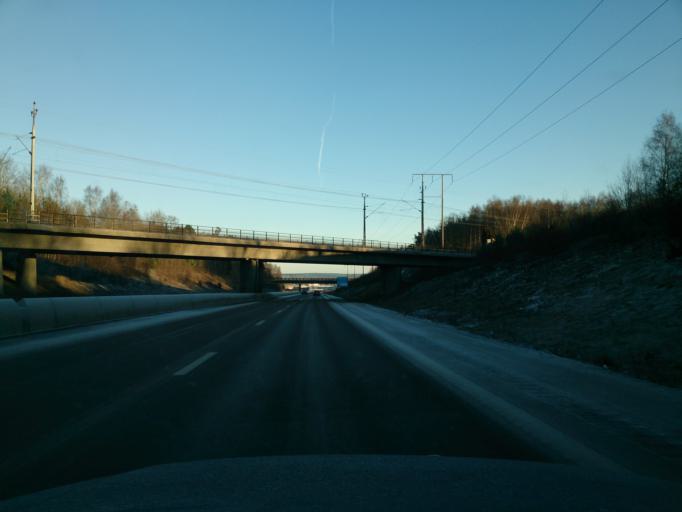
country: SE
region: OEstergoetland
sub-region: Norrkopings Kommun
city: Norrkoping
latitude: 58.6127
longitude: 16.1382
